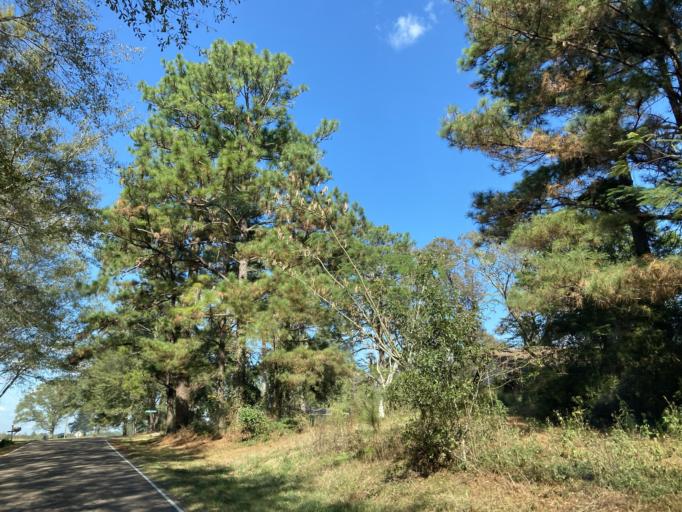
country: US
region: Mississippi
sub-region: Lamar County
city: Sumrall
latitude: 31.2983
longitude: -89.5402
